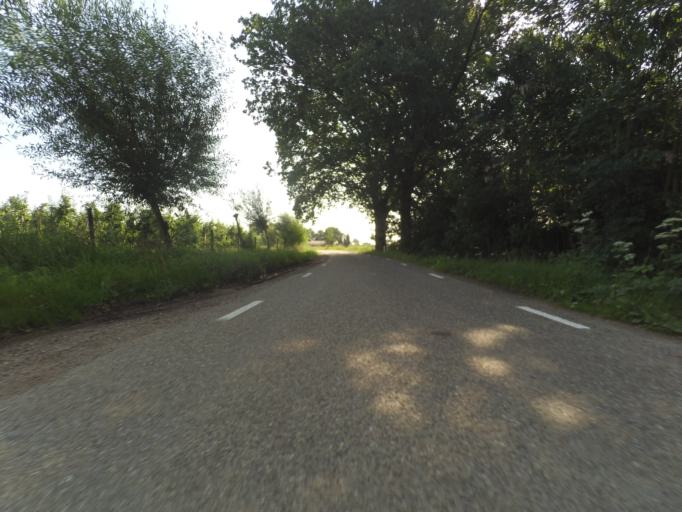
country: NL
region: Gelderland
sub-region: Gemeente Culemborg
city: Culemborg
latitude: 51.9891
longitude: 5.2554
